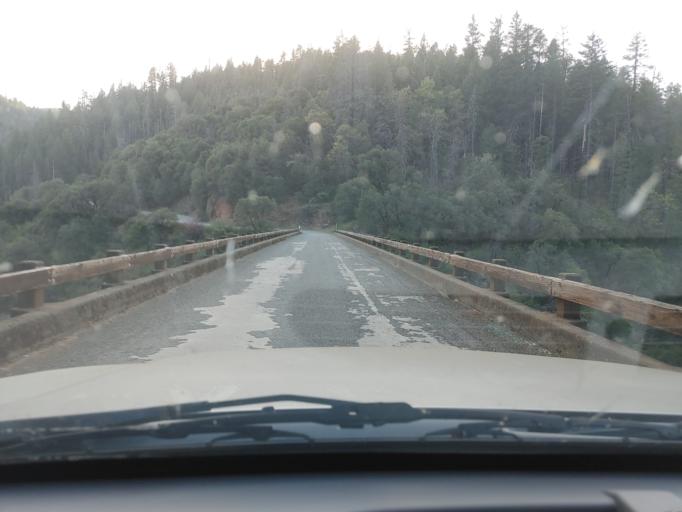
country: US
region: California
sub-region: Shasta County
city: Bella Vista
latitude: 40.8402
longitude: -122.0163
